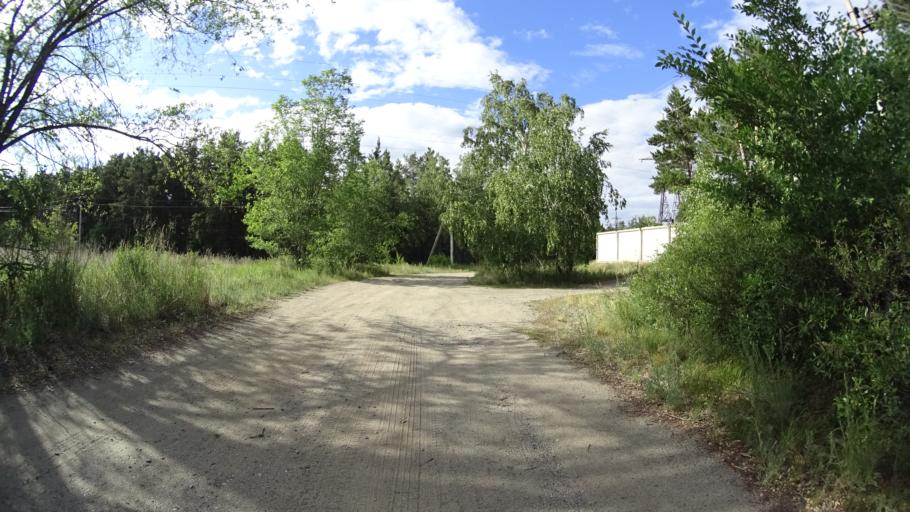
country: RU
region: Chelyabinsk
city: Troitsk
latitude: 54.0510
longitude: 61.6266
